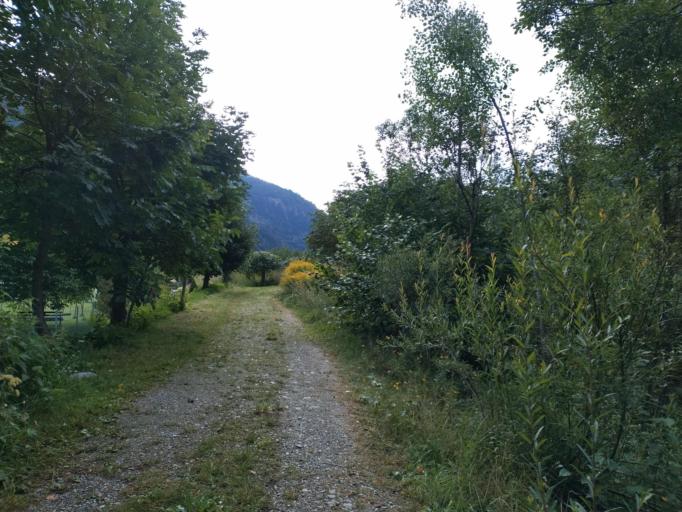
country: AT
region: Tyrol
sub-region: Politischer Bezirk Lienz
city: Hopfgarten in Defereggen
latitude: 46.9299
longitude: 12.5792
